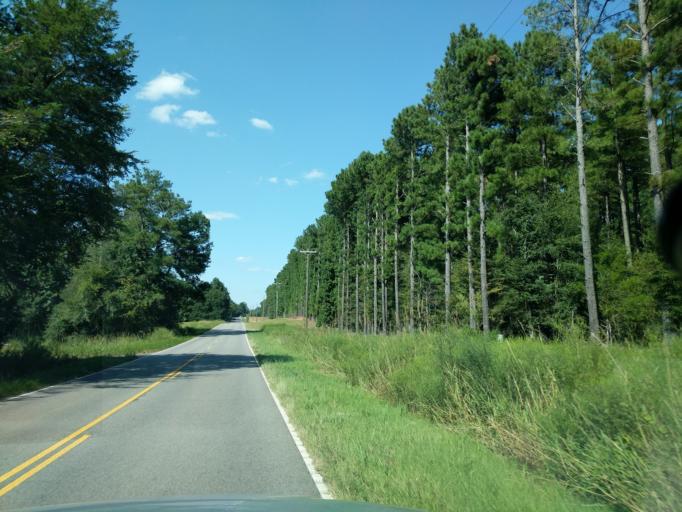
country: US
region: South Carolina
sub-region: Lexington County
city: Leesville
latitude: 33.9728
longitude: -81.5280
